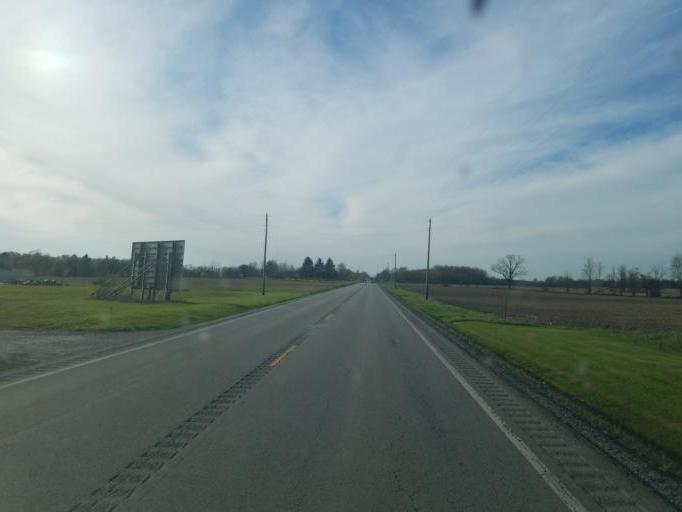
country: US
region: Ohio
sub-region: Huron County
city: Greenwich
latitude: 41.1183
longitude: -82.5092
